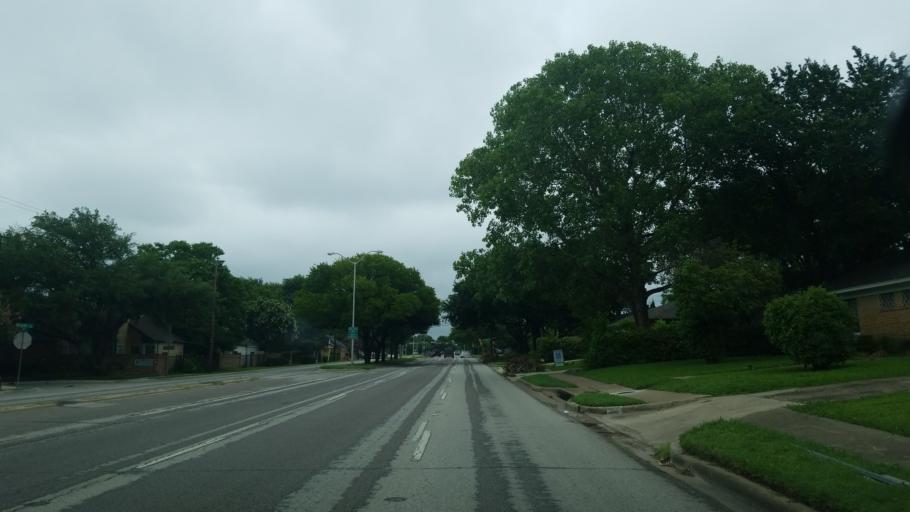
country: US
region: Texas
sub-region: Dallas County
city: Farmers Branch
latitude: 32.8951
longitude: -96.8743
